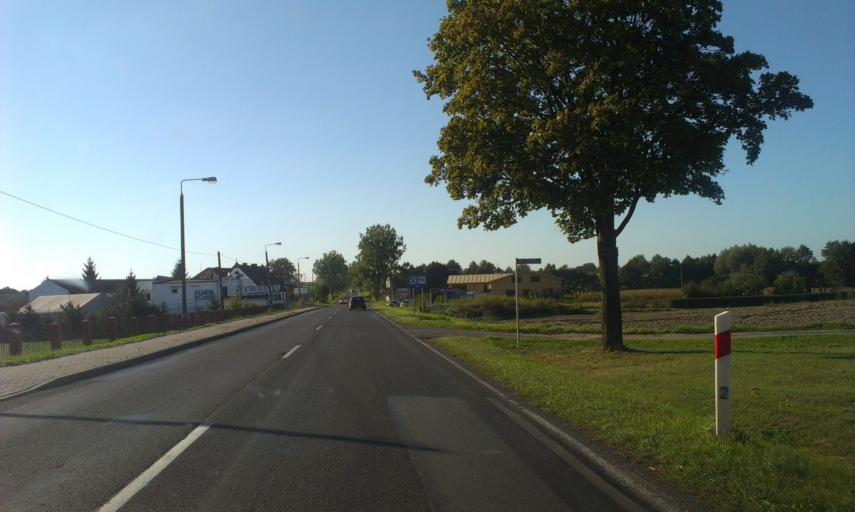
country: PL
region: Kujawsko-Pomorskie
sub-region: Powiat swiecki
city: Bukowiec
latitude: 53.4327
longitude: 18.3054
